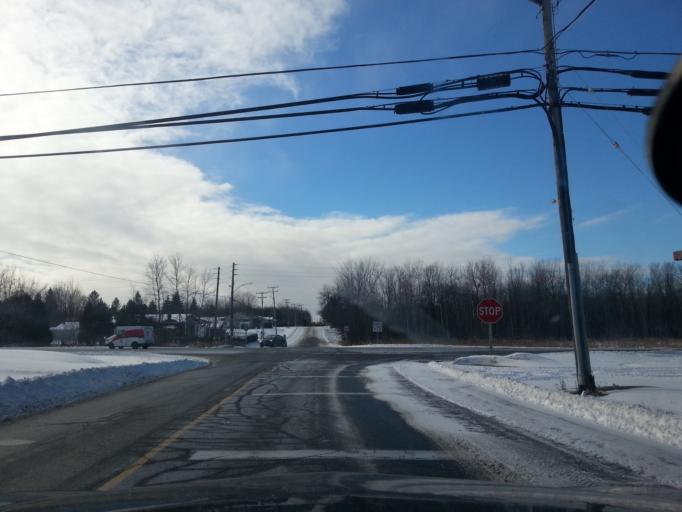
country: CA
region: Ontario
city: Cornwall
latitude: 45.0770
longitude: -74.7815
